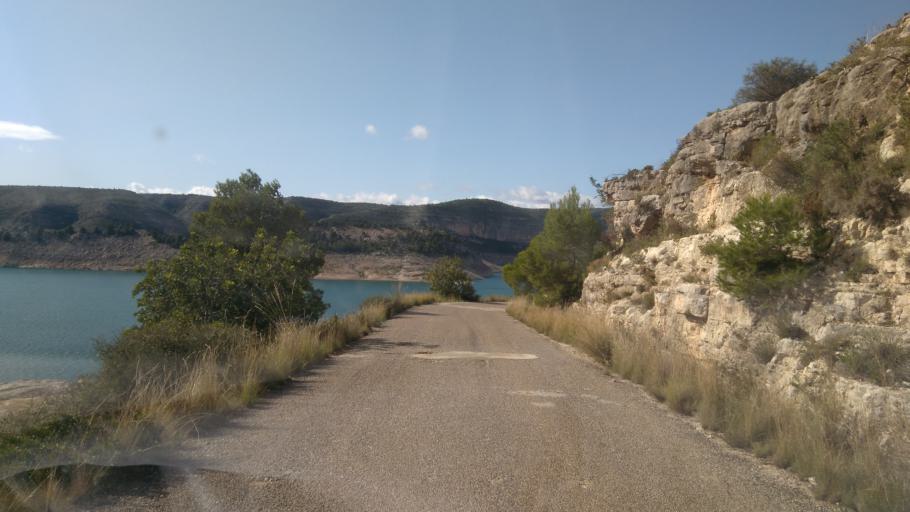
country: ES
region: Valencia
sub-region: Provincia de Valencia
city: Sumacarcer
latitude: 39.1521
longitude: -0.6544
